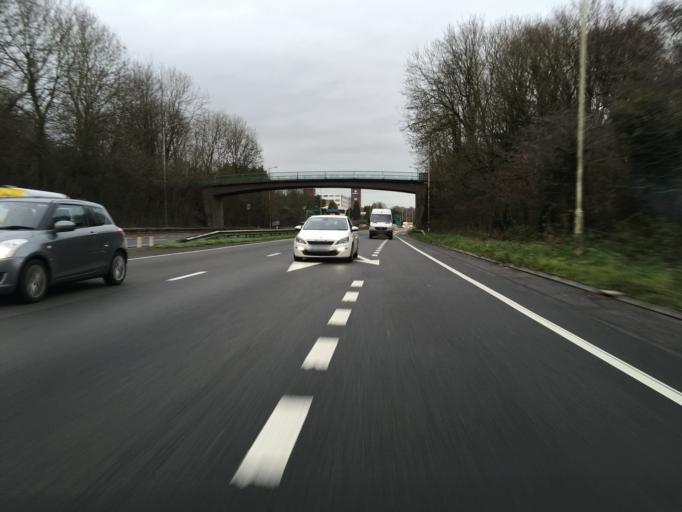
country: GB
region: Wales
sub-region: Cardiff
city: Cardiff
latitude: 51.5242
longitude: -3.1370
